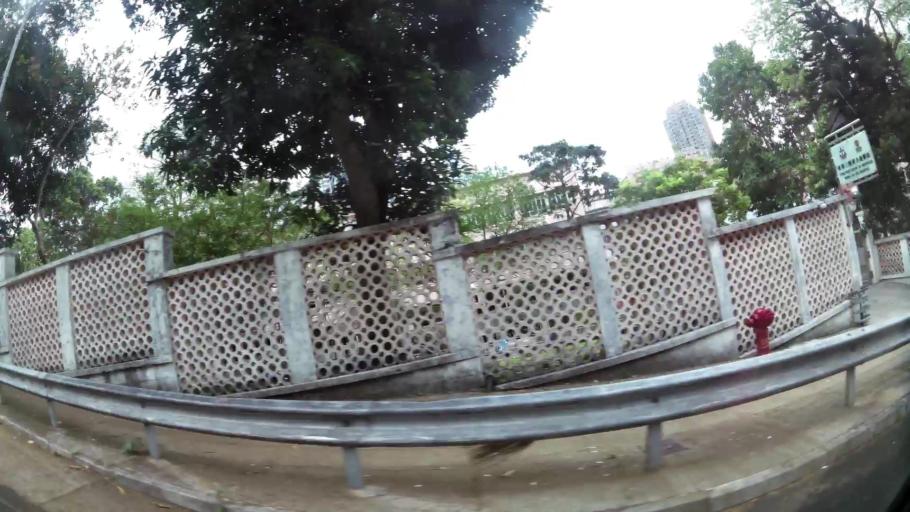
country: HK
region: Wong Tai Sin
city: Wong Tai Sin
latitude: 22.3470
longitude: 114.1959
